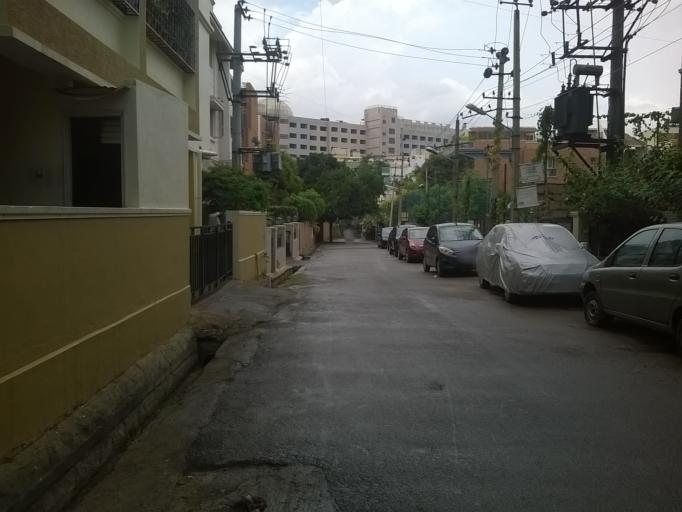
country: IN
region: Karnataka
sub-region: Bangalore Urban
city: Bangalore
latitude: 12.9908
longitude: 77.6615
